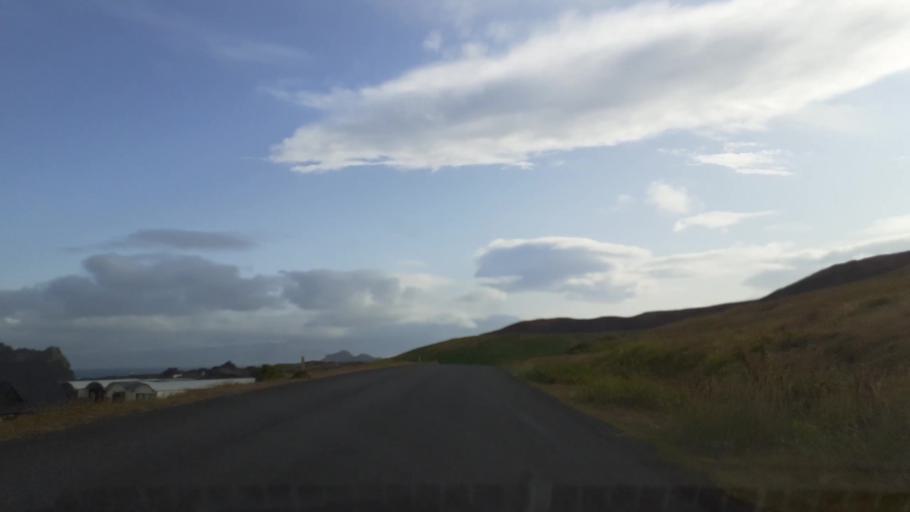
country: IS
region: South
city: Vestmannaeyjar
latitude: 63.4323
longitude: -20.2678
